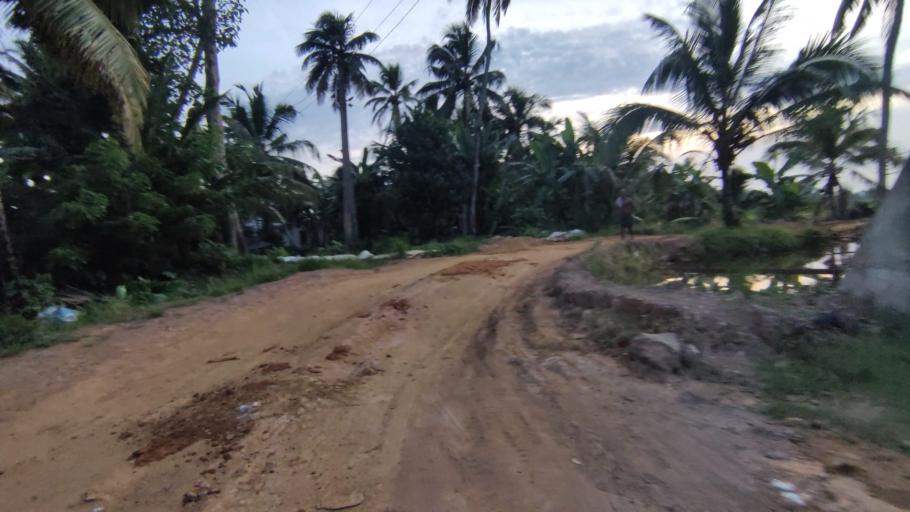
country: IN
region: Kerala
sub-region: Kottayam
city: Kottayam
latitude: 9.6470
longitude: 76.4648
